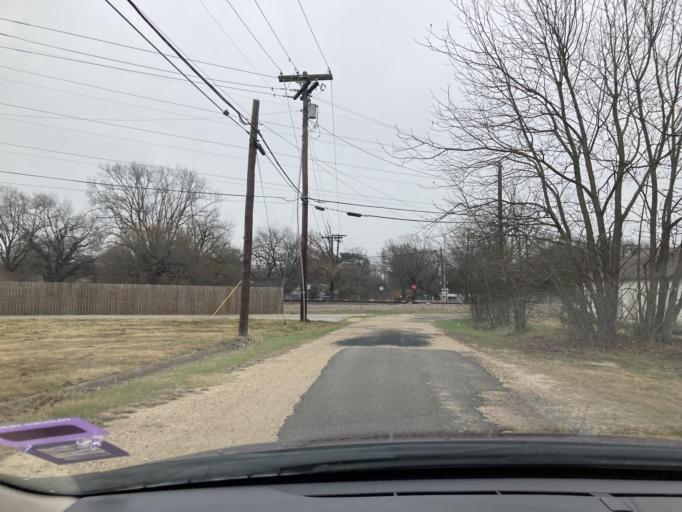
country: US
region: Texas
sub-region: Navarro County
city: Corsicana
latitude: 32.1061
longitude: -96.4746
